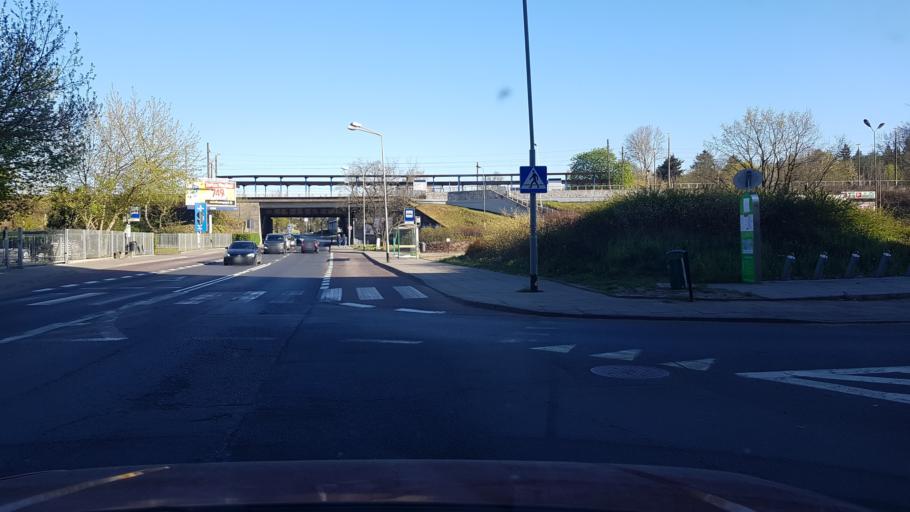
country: PL
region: West Pomeranian Voivodeship
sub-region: Szczecin
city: Szczecin
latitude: 53.3797
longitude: 14.6359
